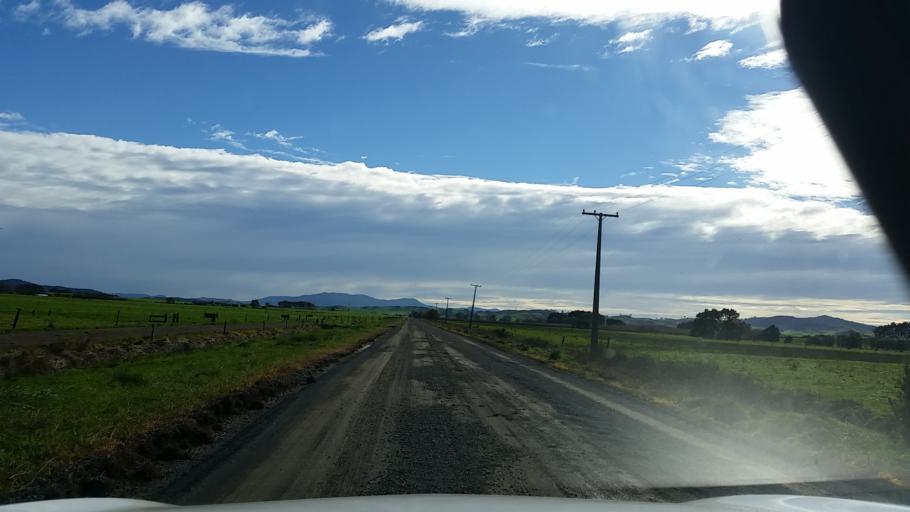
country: NZ
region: Waikato
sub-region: Hamilton City
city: Hamilton
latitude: -37.6409
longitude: 175.4313
